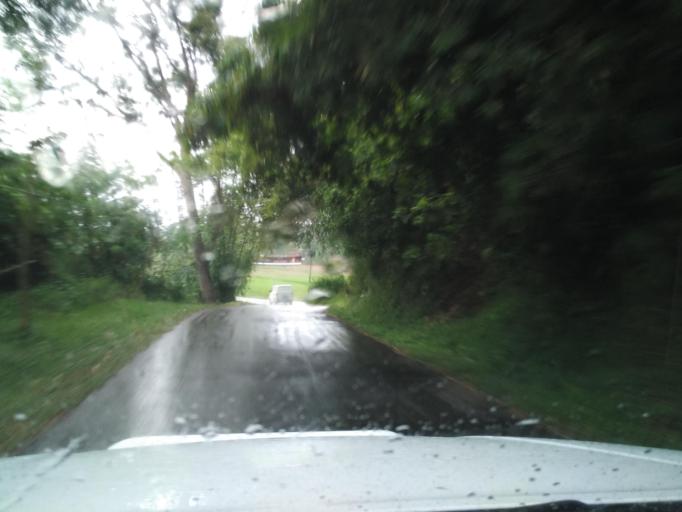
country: ID
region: West Java
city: Ciranjang-hilir
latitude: -6.7079
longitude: 107.1942
